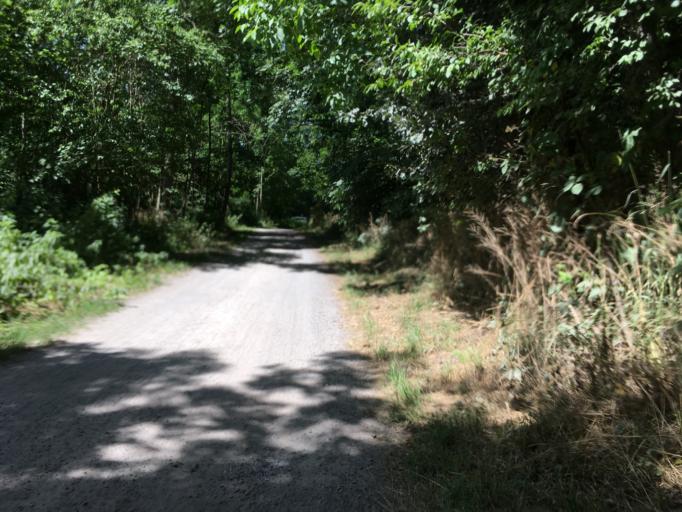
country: DE
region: Baden-Wuerttemberg
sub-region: Regierungsbezirk Stuttgart
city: Oberriexingen
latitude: 48.9248
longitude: 9.0167
